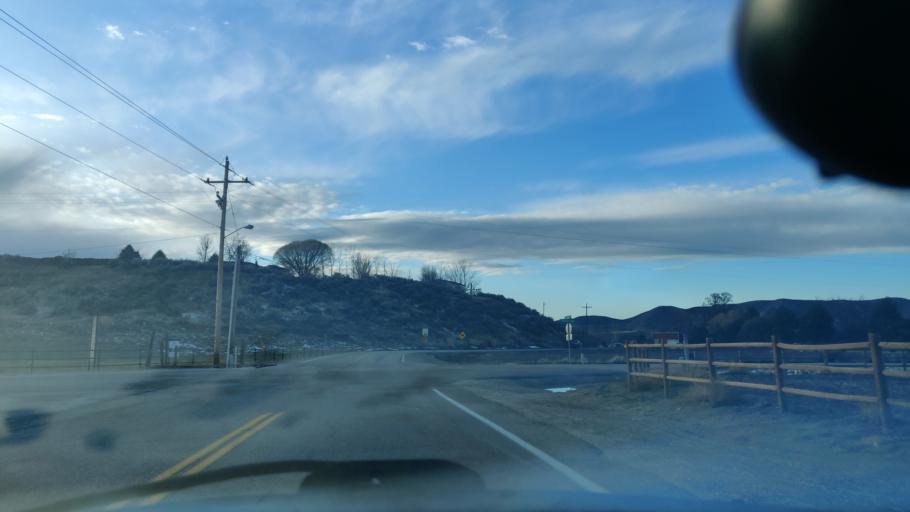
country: US
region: Idaho
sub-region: Ada County
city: Eagle
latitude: 43.7300
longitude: -116.2682
